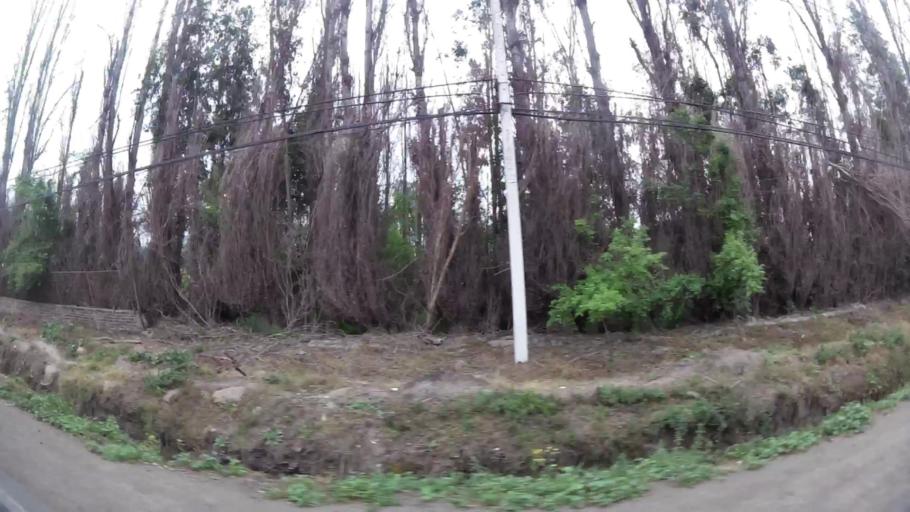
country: CL
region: Santiago Metropolitan
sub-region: Provincia de Chacabuco
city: Lampa
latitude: -33.2436
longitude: -70.7654
